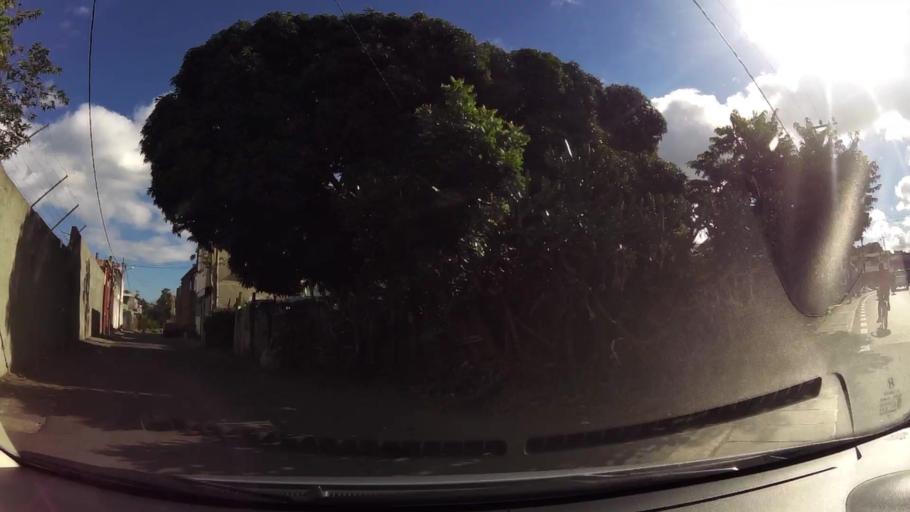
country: MU
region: Pamplemousses
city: Le Hochet
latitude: -20.1502
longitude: 57.5159
